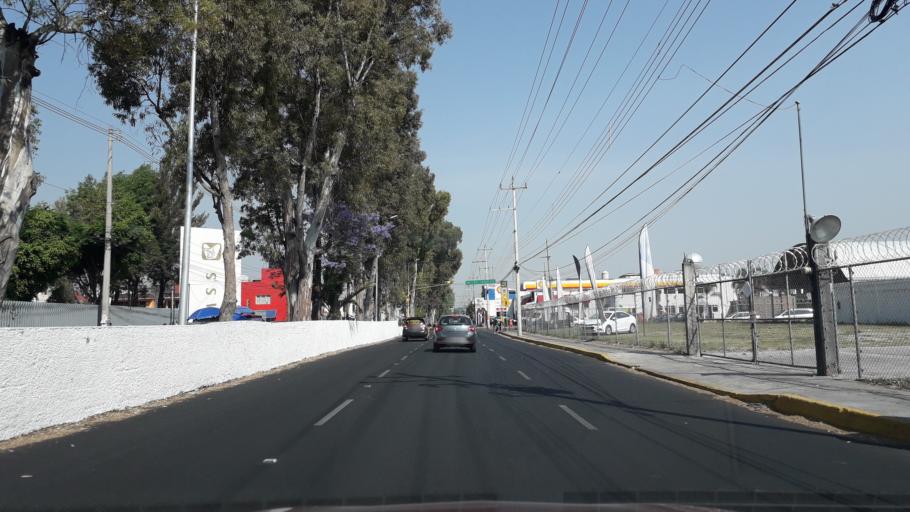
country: MX
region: Puebla
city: Puebla
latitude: 19.0664
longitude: -98.2160
